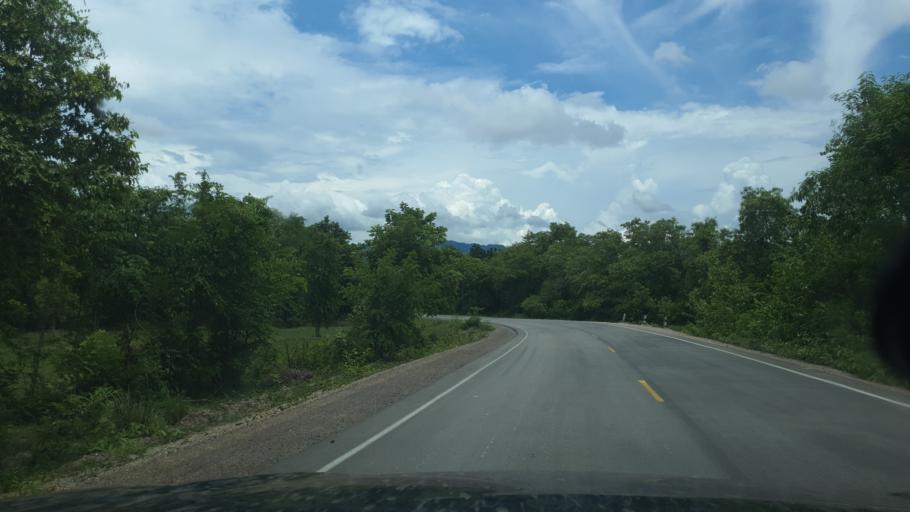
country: TH
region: Lampang
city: Sop Prap
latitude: 17.9301
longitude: 99.3712
